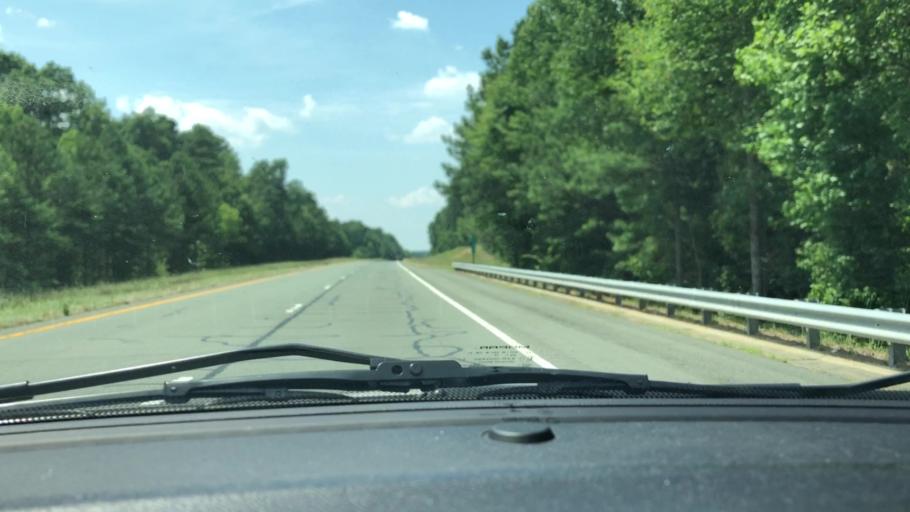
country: US
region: North Carolina
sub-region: Chatham County
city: Siler City
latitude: 35.7850
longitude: -79.5173
